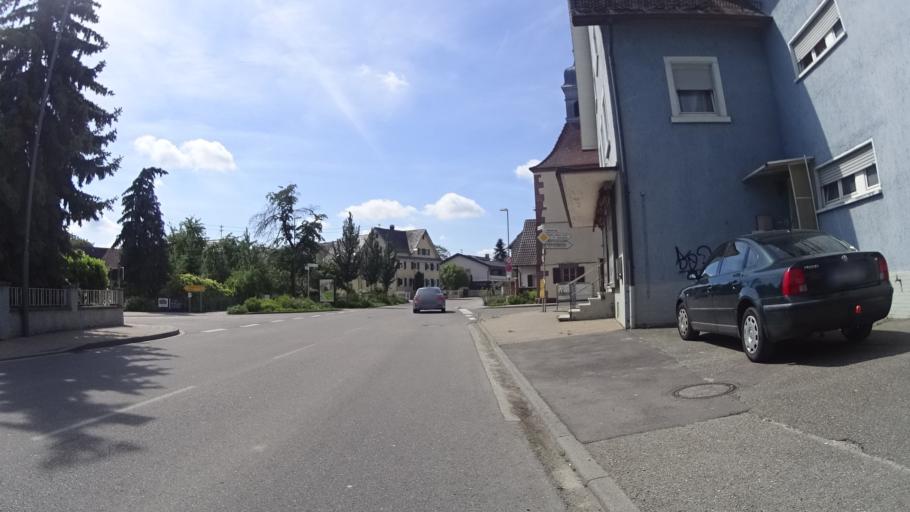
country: DE
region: Baden-Wuerttemberg
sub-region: Freiburg Region
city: Meissenheim
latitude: 48.4662
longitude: 7.8140
